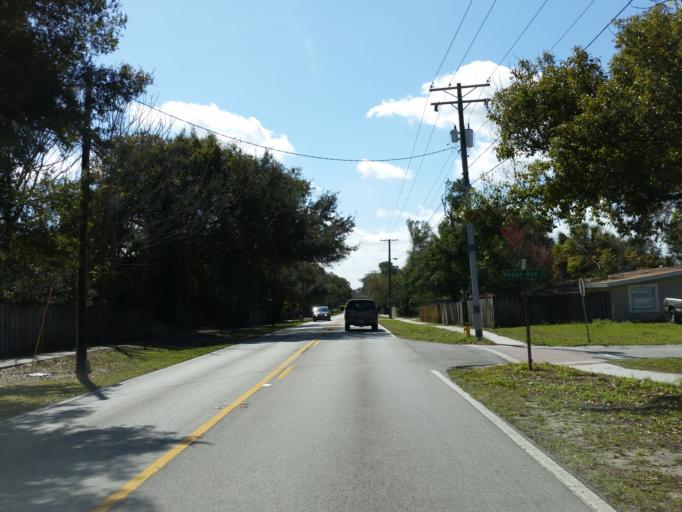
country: US
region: Florida
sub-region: Hillsborough County
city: Brandon
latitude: 27.9508
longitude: -82.2776
